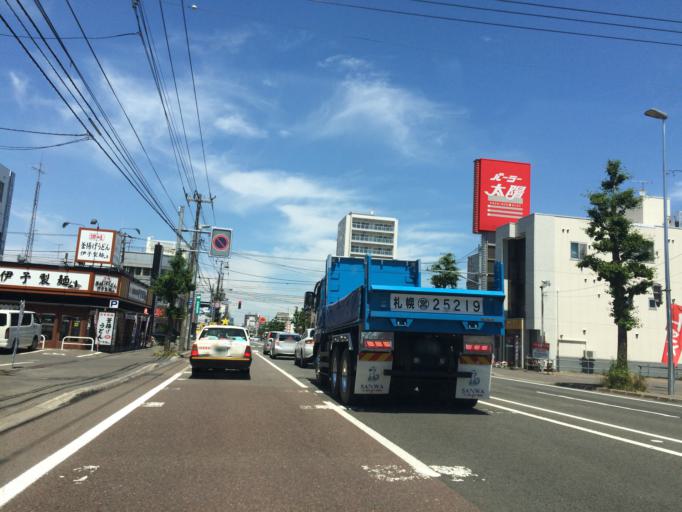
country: JP
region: Hokkaido
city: Sapporo
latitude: 43.0301
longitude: 141.3449
